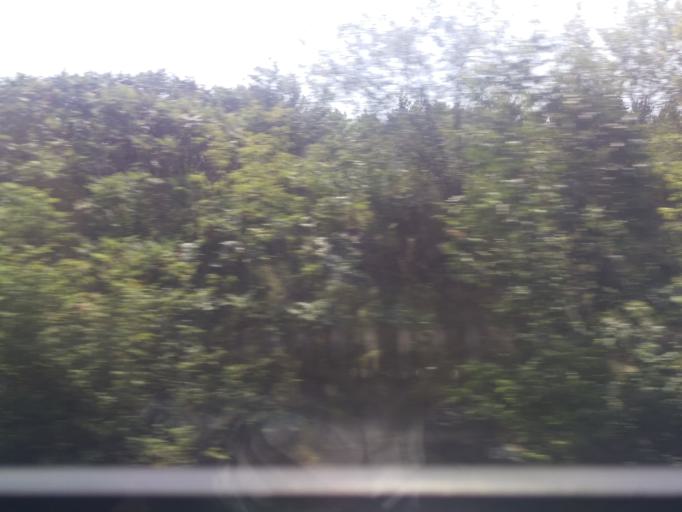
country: CA
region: Ontario
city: Kingston
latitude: 44.2583
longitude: -76.4933
